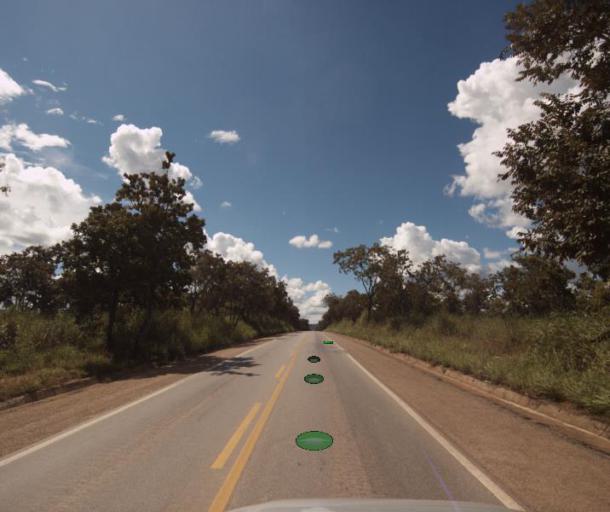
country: BR
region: Goias
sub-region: Porangatu
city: Porangatu
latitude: -13.6940
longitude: -49.0222
